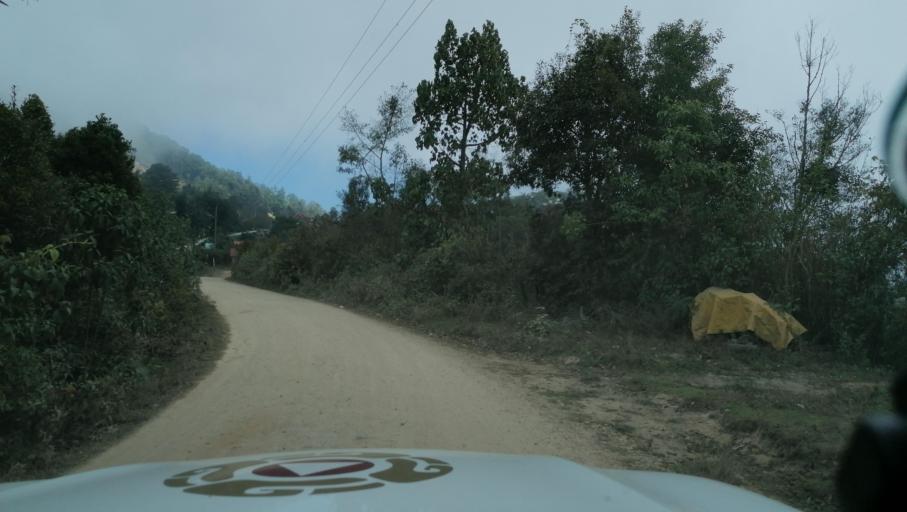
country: MX
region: Chiapas
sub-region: Tapachula
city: Canton Villaflor
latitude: 15.2101
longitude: -92.2403
